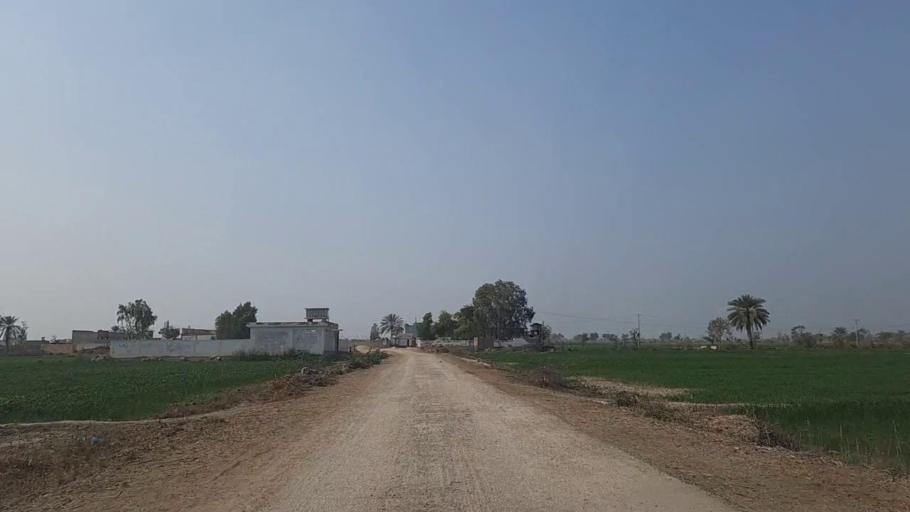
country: PK
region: Sindh
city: Daur
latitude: 26.4488
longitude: 68.4444
